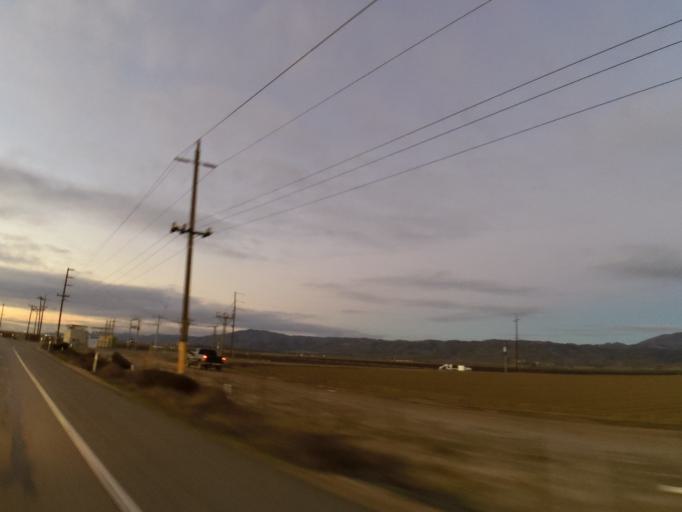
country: US
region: California
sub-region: Monterey County
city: Greenfield
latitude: 36.3652
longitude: -121.2793
